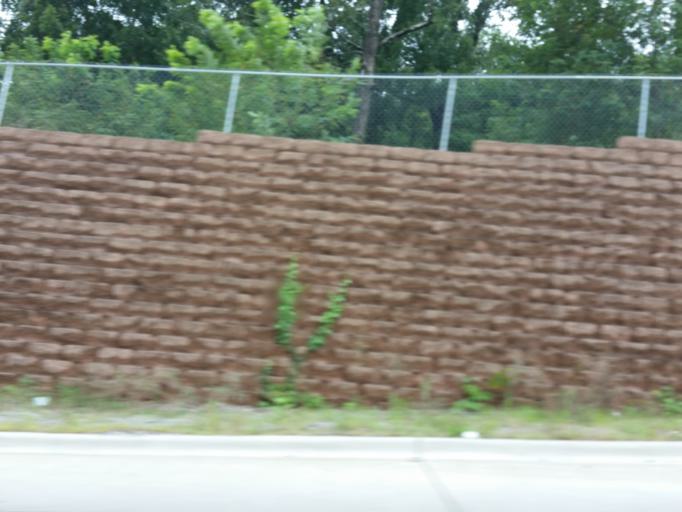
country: US
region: Missouri
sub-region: Cape Girardeau County
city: Cape Girardeau
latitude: 37.3310
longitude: -89.5450
